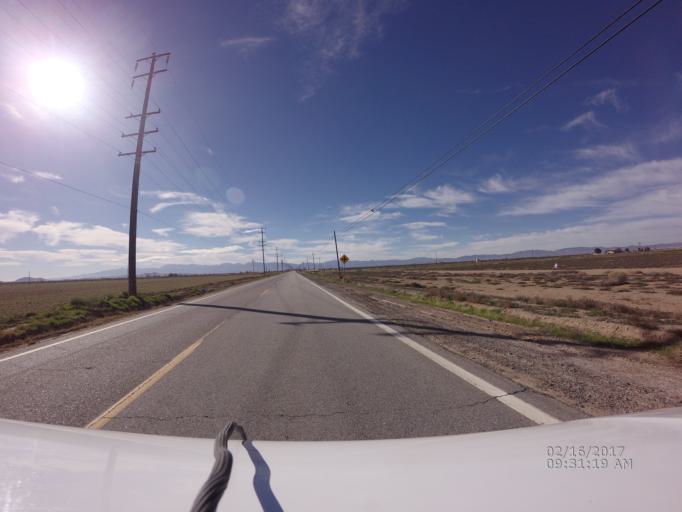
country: US
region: California
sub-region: Kern County
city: Edwards Air Force Base
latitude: 34.7509
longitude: -117.9699
